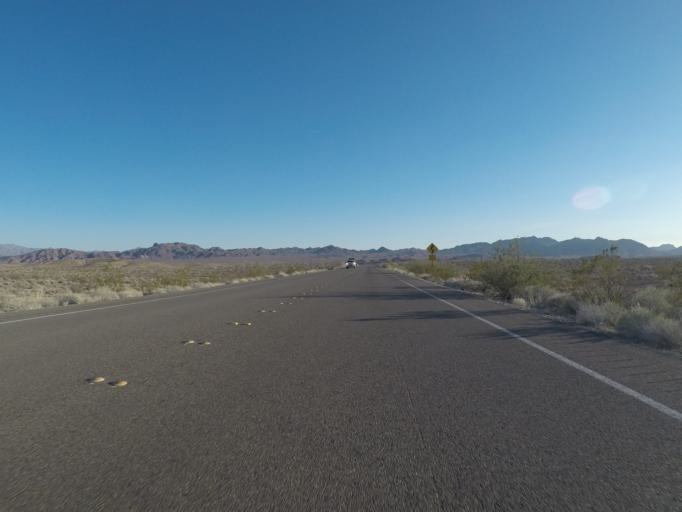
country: US
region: Nevada
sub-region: Clark County
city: Moapa Valley
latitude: 36.3191
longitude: -114.4923
